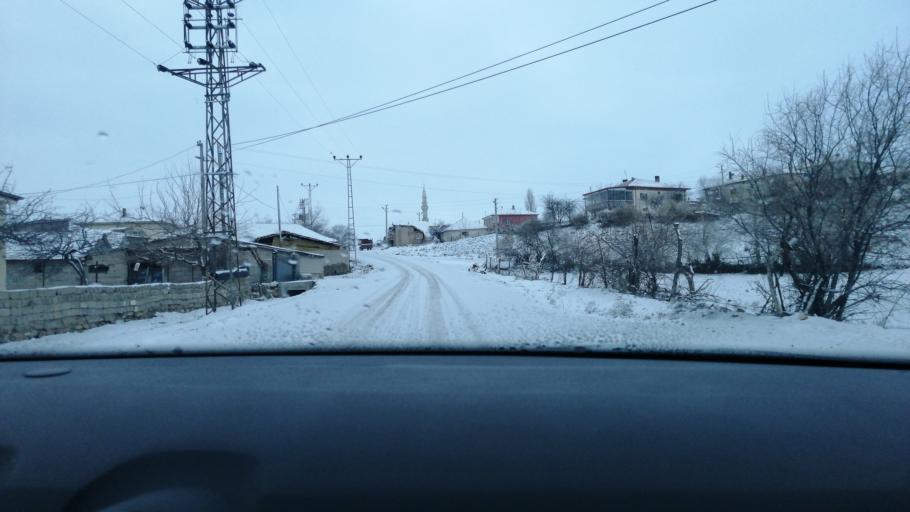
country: TR
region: Aksaray
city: Agacoren
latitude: 38.9359
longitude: 33.9485
